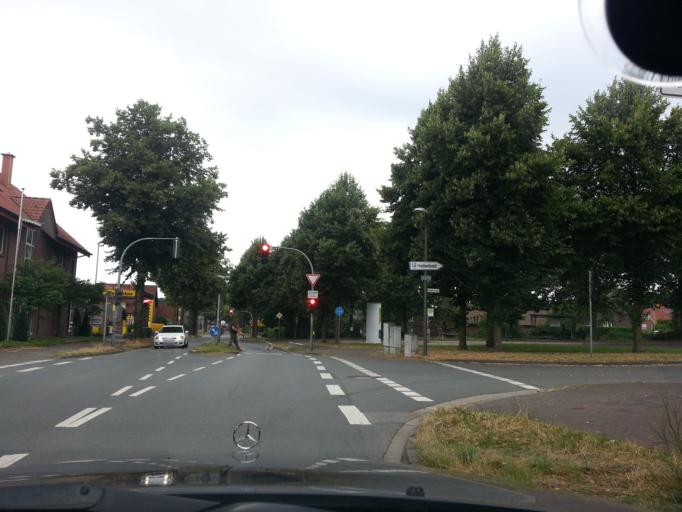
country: DE
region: North Rhine-Westphalia
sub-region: Regierungsbezirk Munster
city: Klein Reken
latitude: 51.7605
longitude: 7.0014
